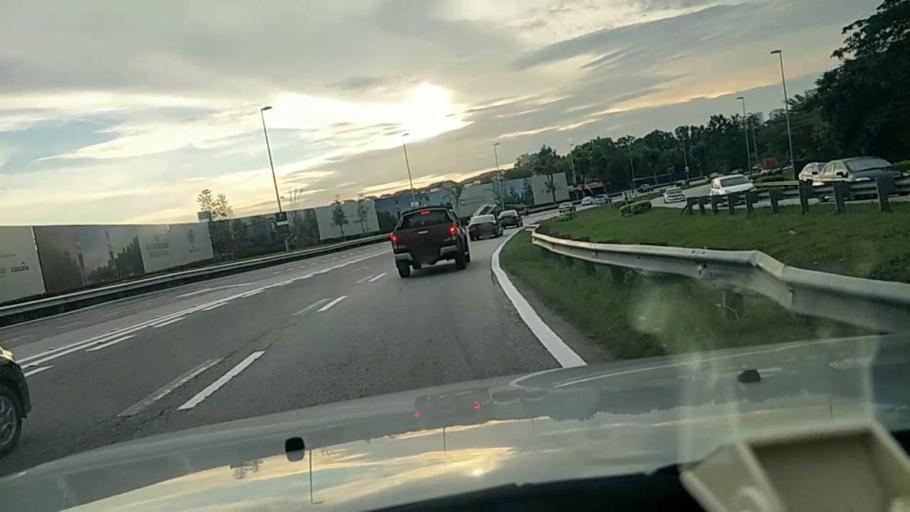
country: MY
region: Selangor
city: Shah Alam
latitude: 3.0995
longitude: 101.4767
